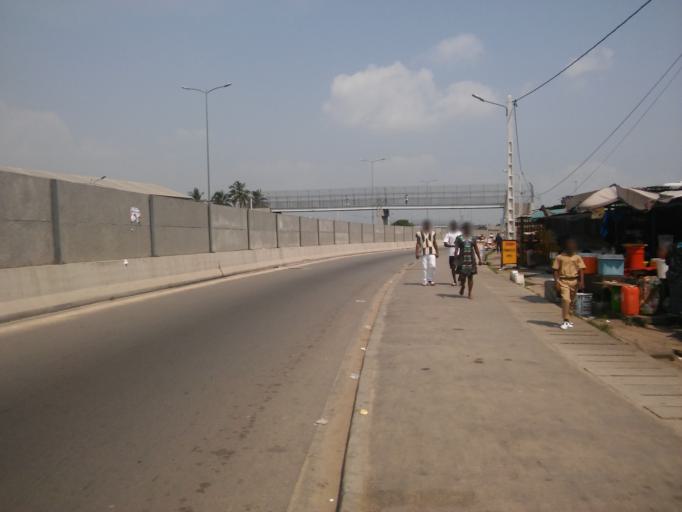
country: CI
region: Lagunes
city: Abidjan
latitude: 5.2983
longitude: -3.9801
